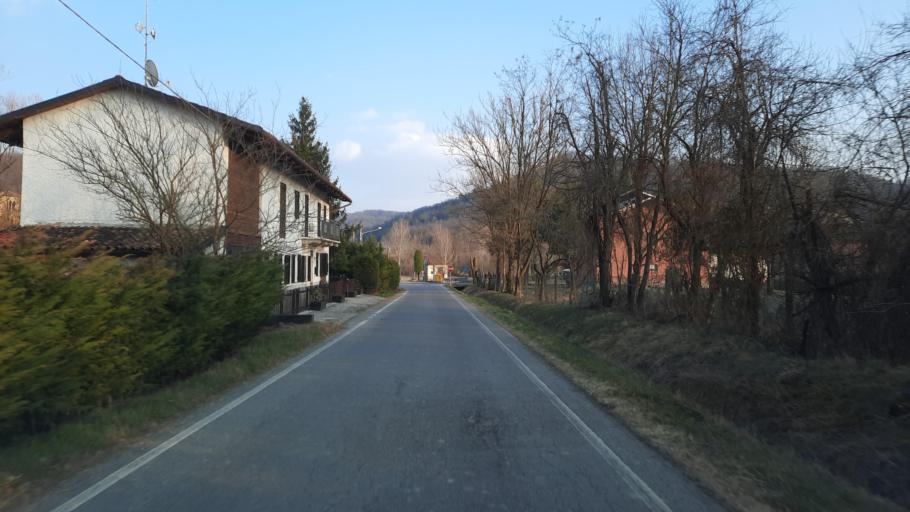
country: IT
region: Piedmont
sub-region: Provincia di Alessandria
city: Odalengo Grande
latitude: 45.0953
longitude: 8.1847
